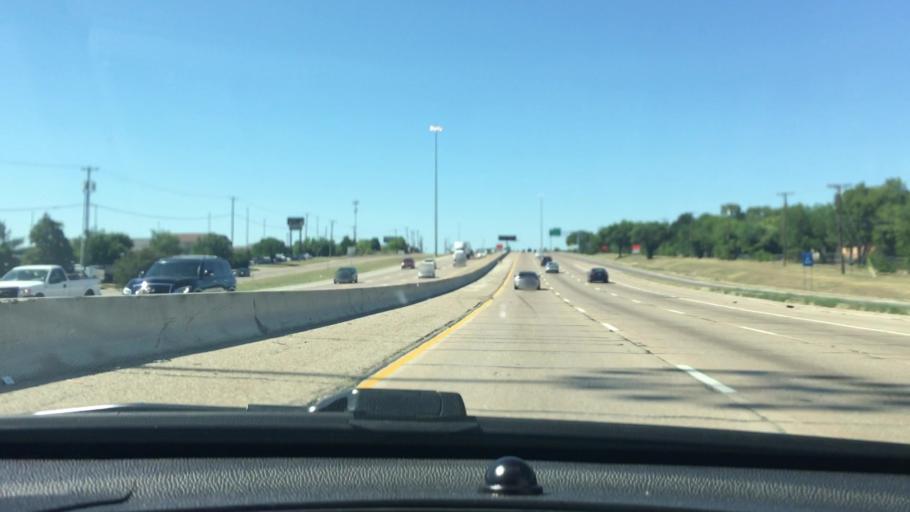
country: US
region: Texas
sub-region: Dallas County
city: Cockrell Hill
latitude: 32.6925
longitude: -96.8231
